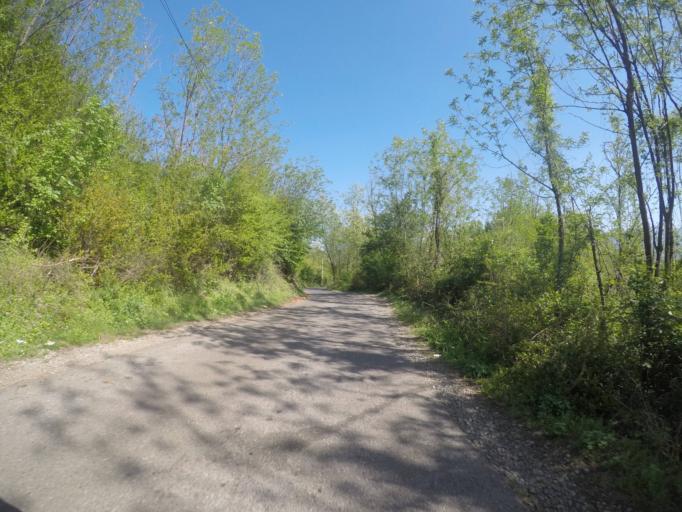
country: ME
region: Danilovgrad
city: Danilovgrad
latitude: 42.5373
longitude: 19.0903
